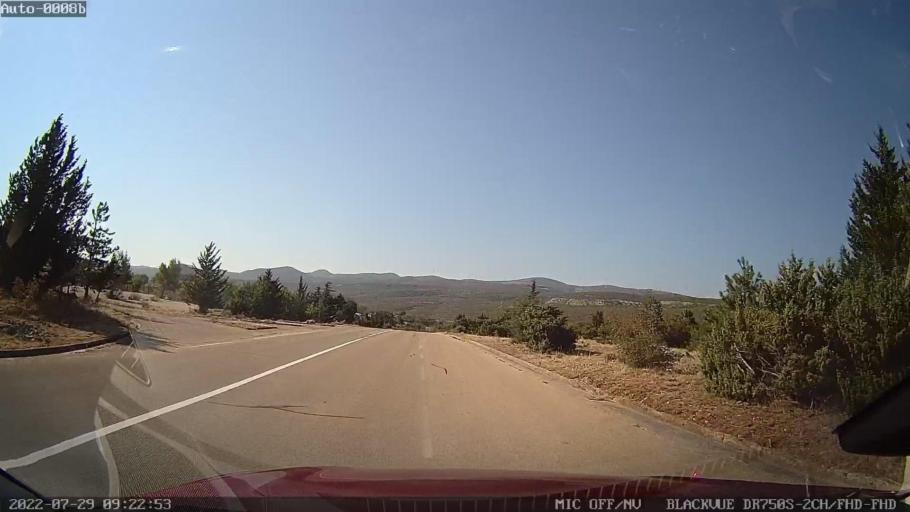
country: HR
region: Zadarska
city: Obrovac
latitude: 44.2118
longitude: 15.6682
